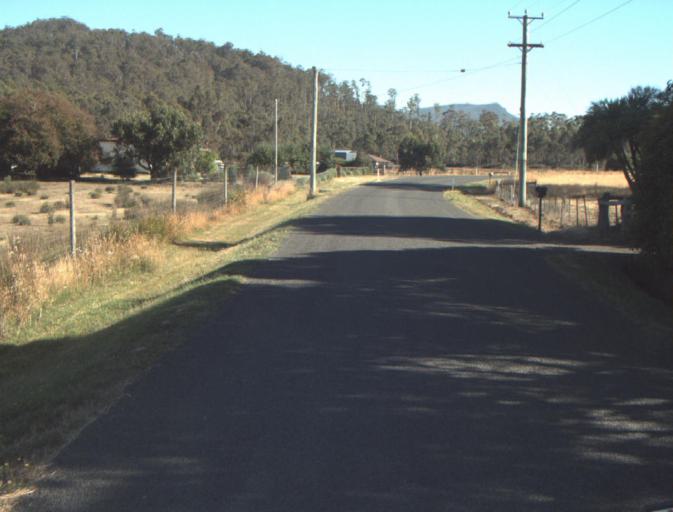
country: AU
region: Tasmania
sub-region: Launceston
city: Newstead
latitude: -41.3766
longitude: 147.2963
